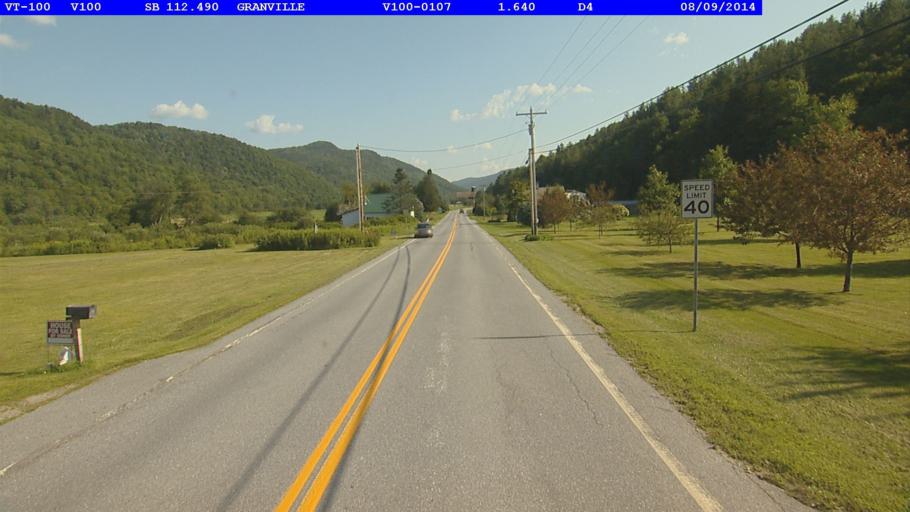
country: US
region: Vermont
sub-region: Orange County
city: Randolph
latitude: 43.9679
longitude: -72.8428
